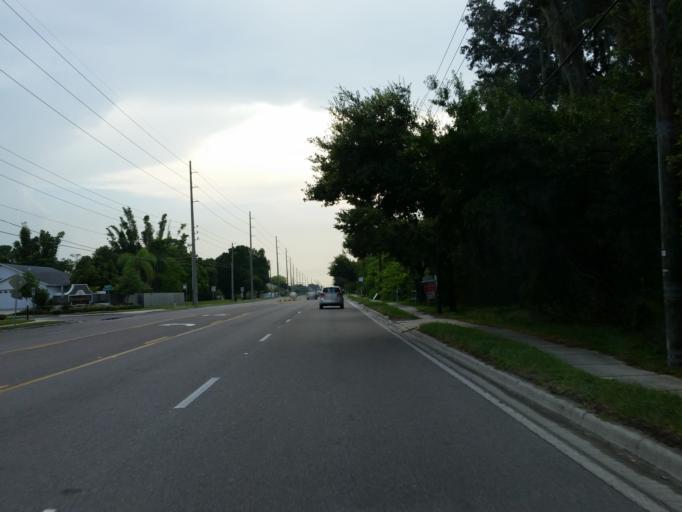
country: US
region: Florida
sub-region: Hillsborough County
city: Riverview
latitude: 27.8937
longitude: -82.3247
